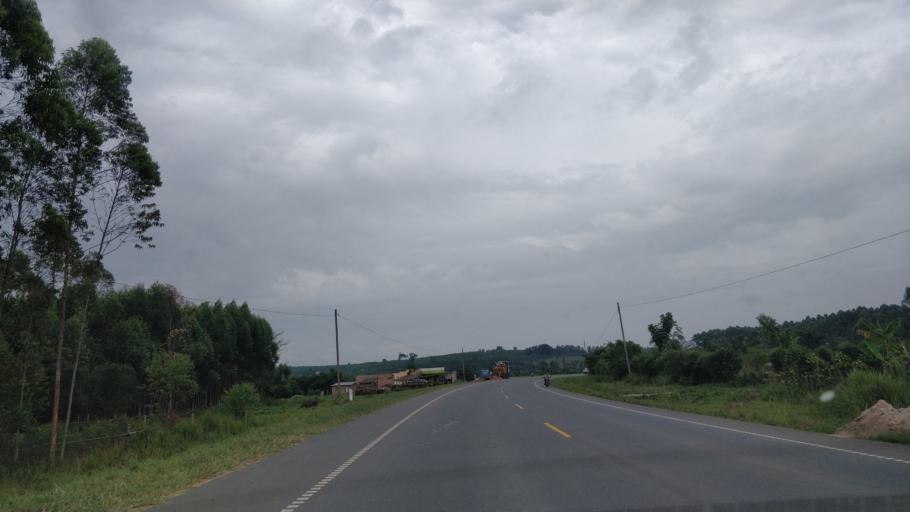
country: UG
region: Western Region
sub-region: Sheema District
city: Kibingo
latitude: -0.6508
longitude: 30.4850
